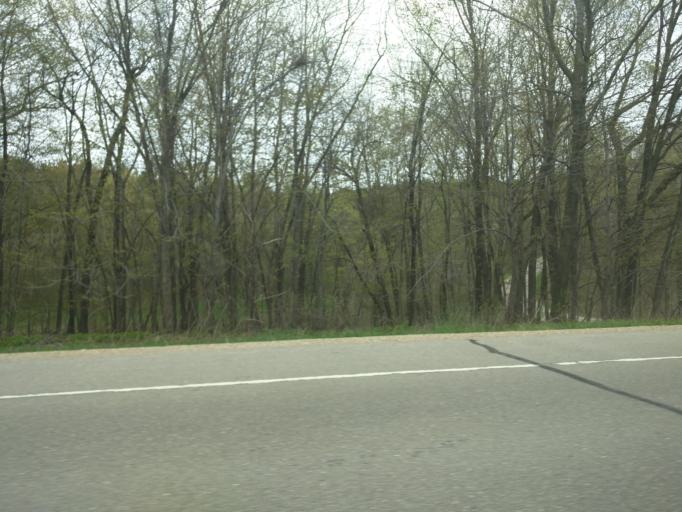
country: US
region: Minnesota
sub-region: Goodhue County
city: Red Wing
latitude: 44.5858
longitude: -92.3801
